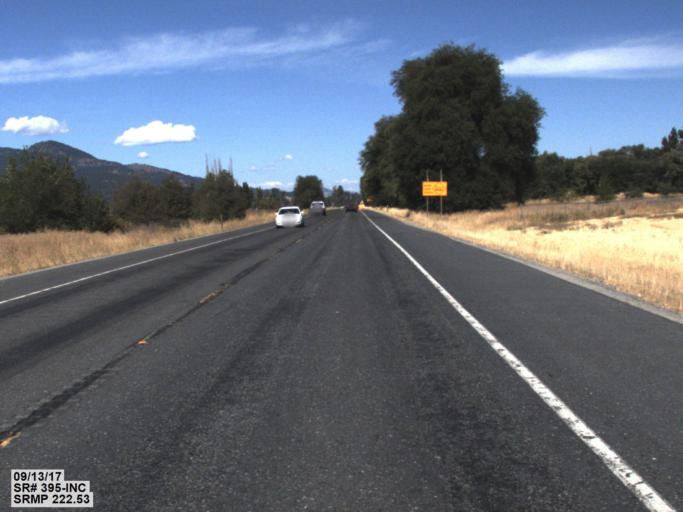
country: US
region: Washington
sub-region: Stevens County
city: Colville
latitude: 48.4492
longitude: -117.8734
